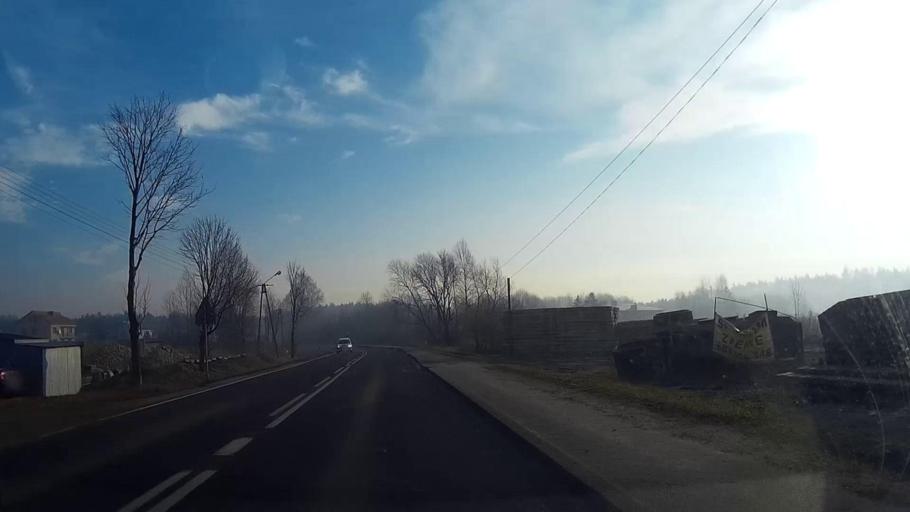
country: PL
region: Lesser Poland Voivodeship
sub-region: Powiat chrzanowski
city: Zarki
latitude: 50.0816
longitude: 19.3617
